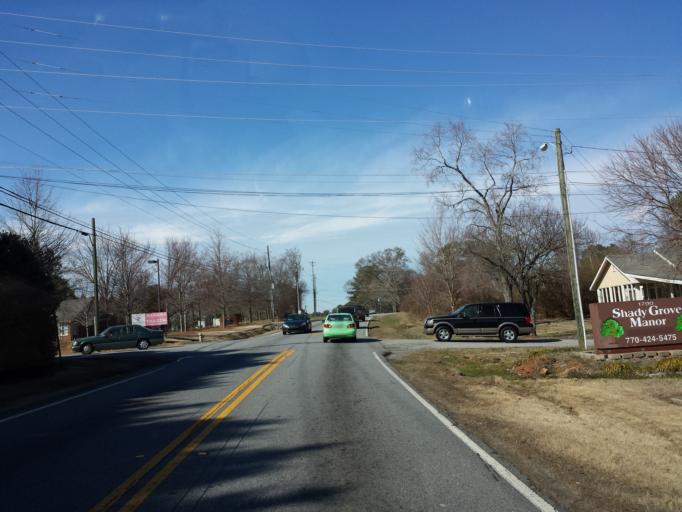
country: US
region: Georgia
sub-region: Cobb County
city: Kennesaw
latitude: 33.9971
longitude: -84.5992
